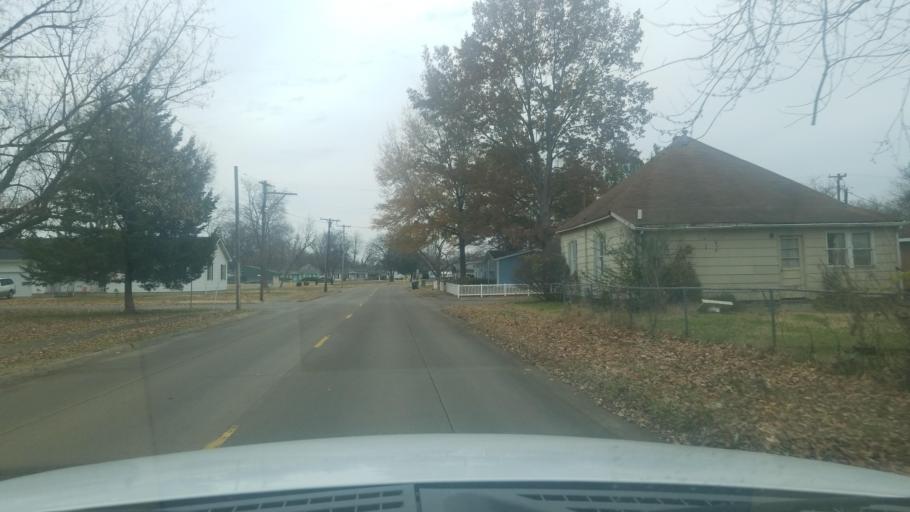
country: US
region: Illinois
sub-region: Saline County
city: Harrisburg
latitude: 37.7341
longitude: -88.5528
